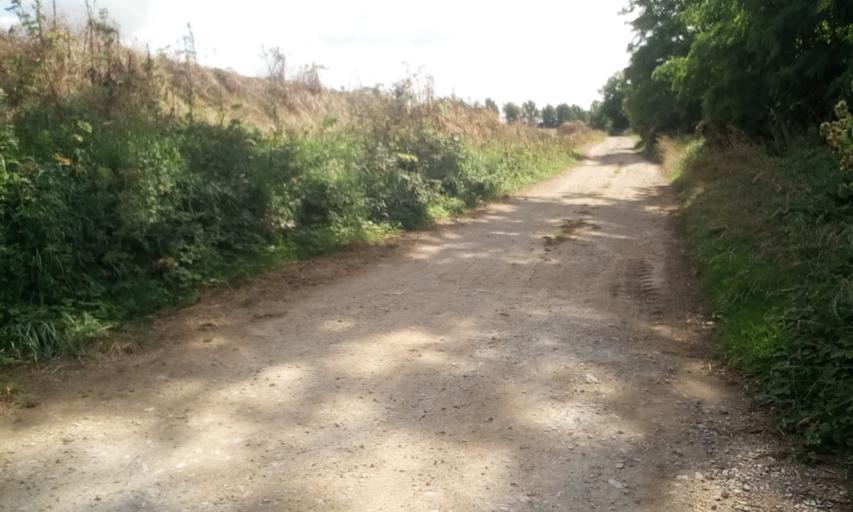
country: FR
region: Lower Normandy
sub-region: Departement du Calvados
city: Moult
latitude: 49.0992
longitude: -0.1889
